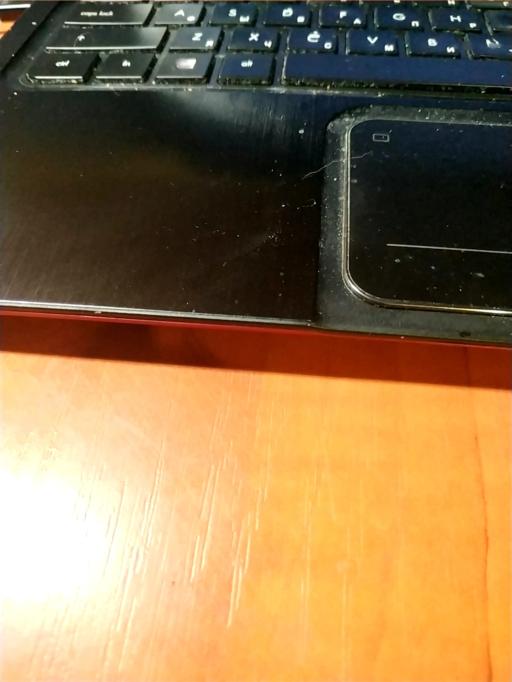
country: RU
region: Tverskaya
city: Ves'yegonsk
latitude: 58.7983
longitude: 37.5436
